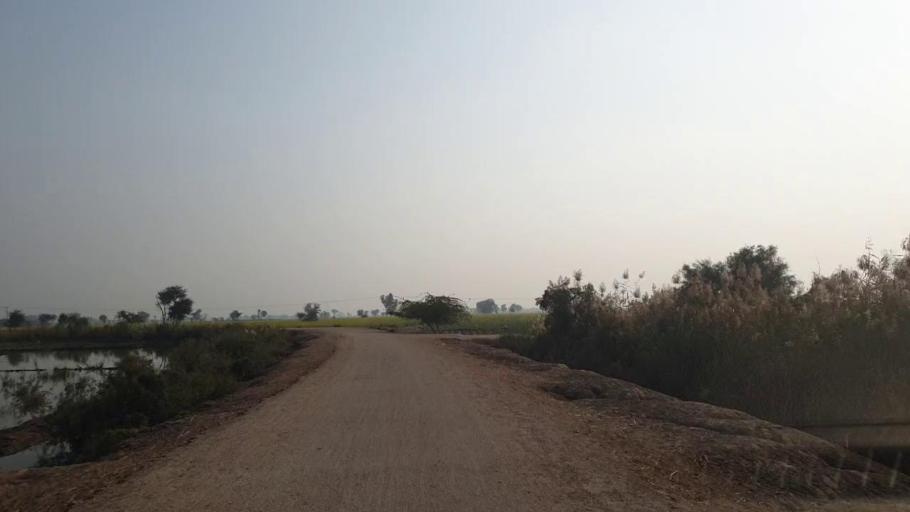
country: PK
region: Sindh
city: Shahdadpur
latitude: 25.9618
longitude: 68.5242
